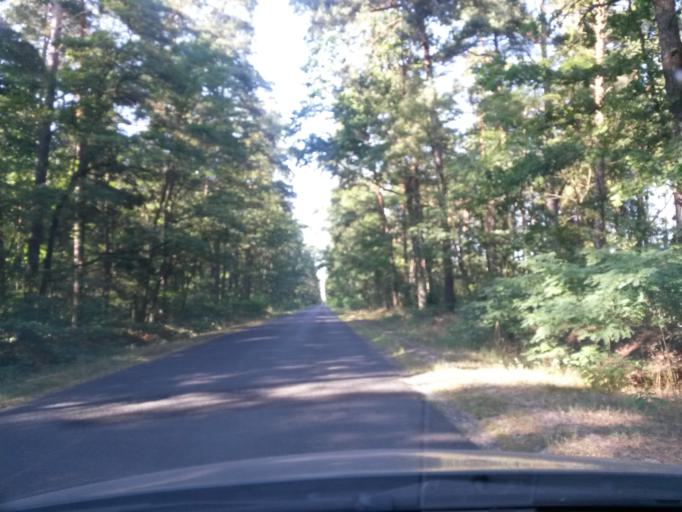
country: PL
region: Kujawsko-Pomorskie
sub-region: Powiat rypinski
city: Skrwilno
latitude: 52.9961
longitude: 19.6280
